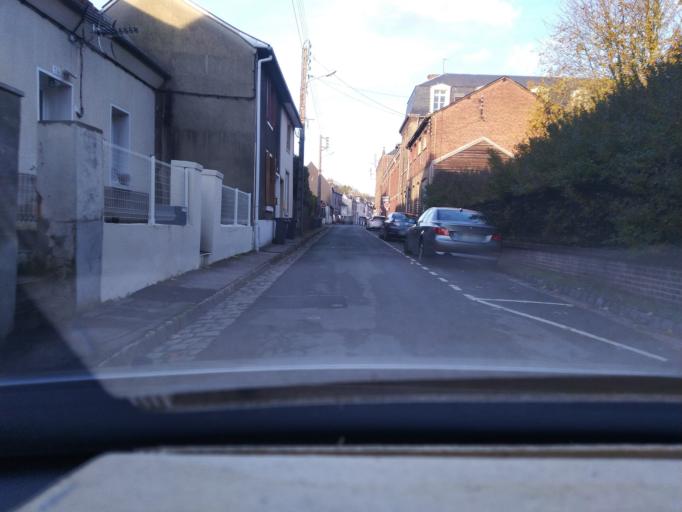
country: FR
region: Haute-Normandie
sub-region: Departement de la Seine-Maritime
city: Darnetal
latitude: 49.4380
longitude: 1.1420
